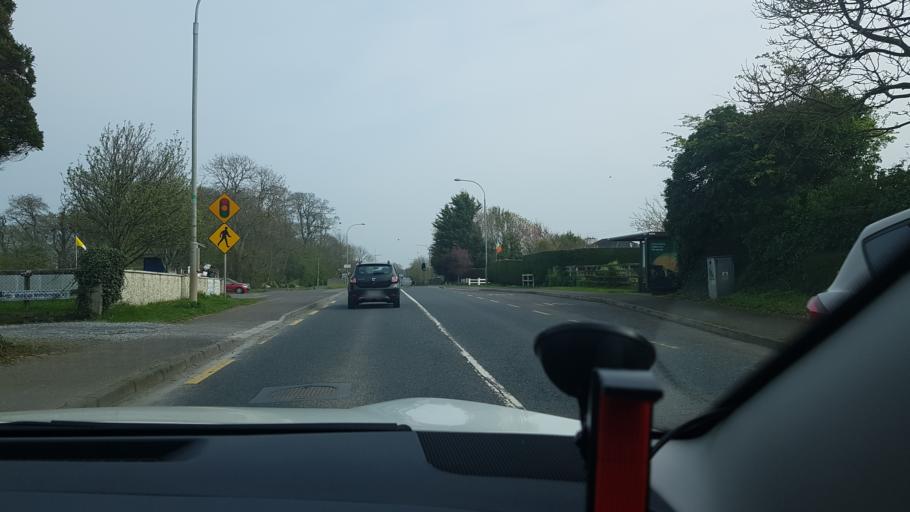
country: IE
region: Leinster
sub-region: An Mhi
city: Stamullin
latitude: 53.6684
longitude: -6.2792
